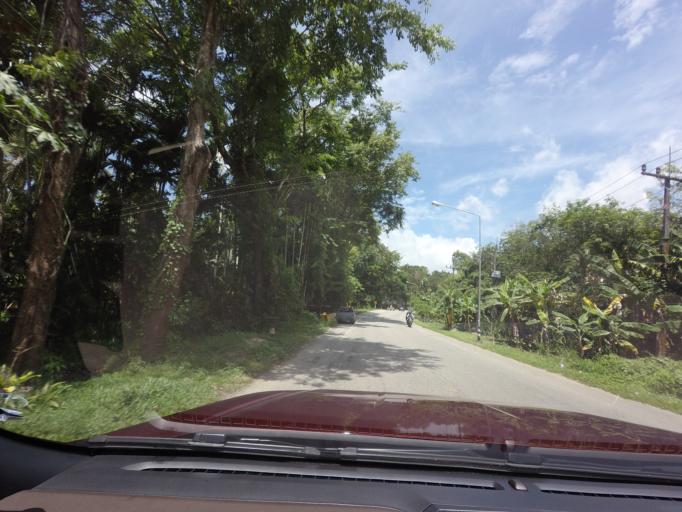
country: TH
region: Narathiwat
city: Ra-ngae
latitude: 6.2457
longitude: 101.6839
